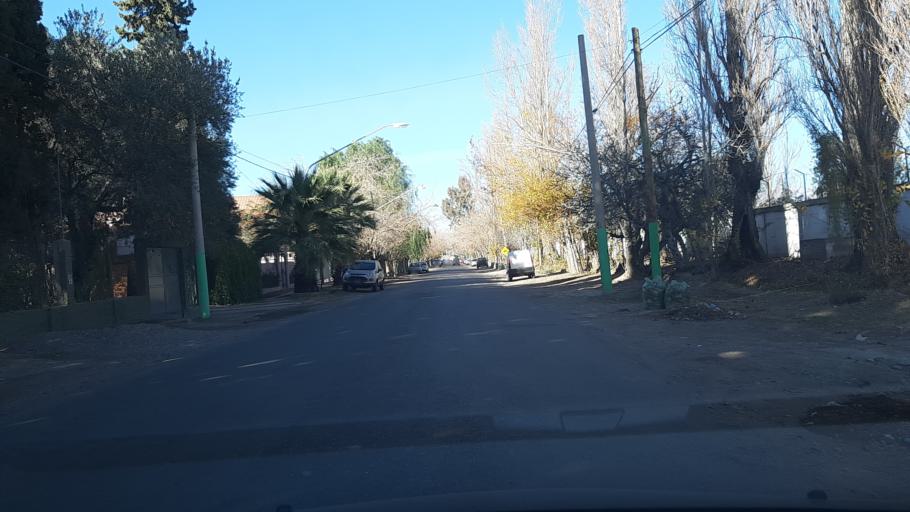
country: AR
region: San Juan
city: San Juan
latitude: -31.5272
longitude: -68.5918
